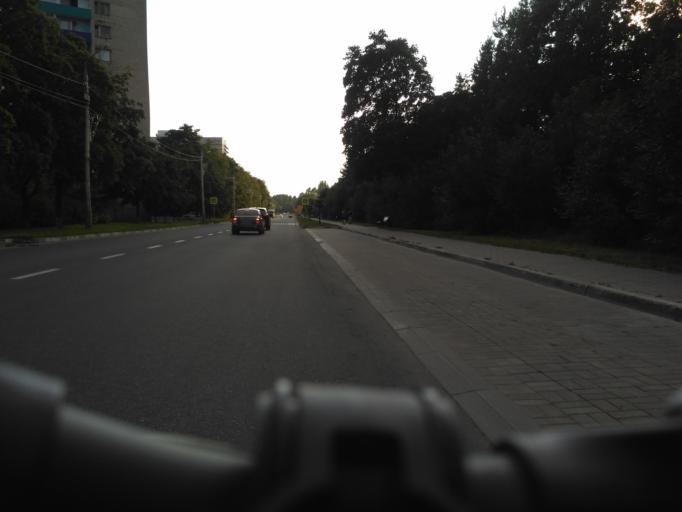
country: RU
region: Moskovskaya
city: Dubna
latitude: 56.7459
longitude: 37.1783
